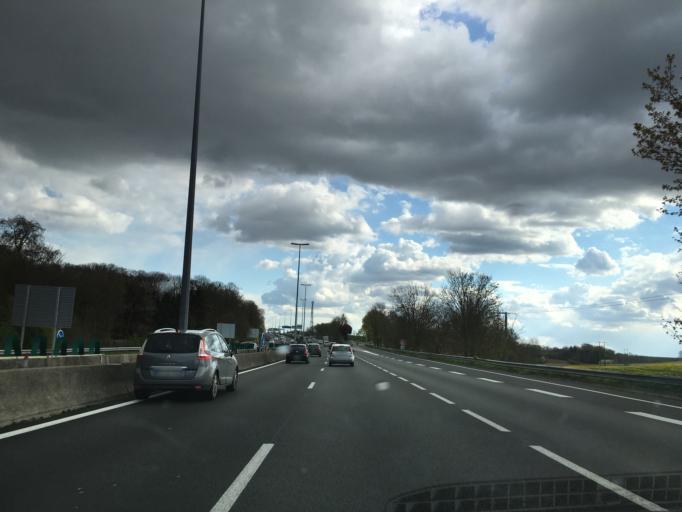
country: FR
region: Ile-de-France
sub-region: Departement du Val-d'Oise
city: Vemars
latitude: 49.0440
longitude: 2.5445
